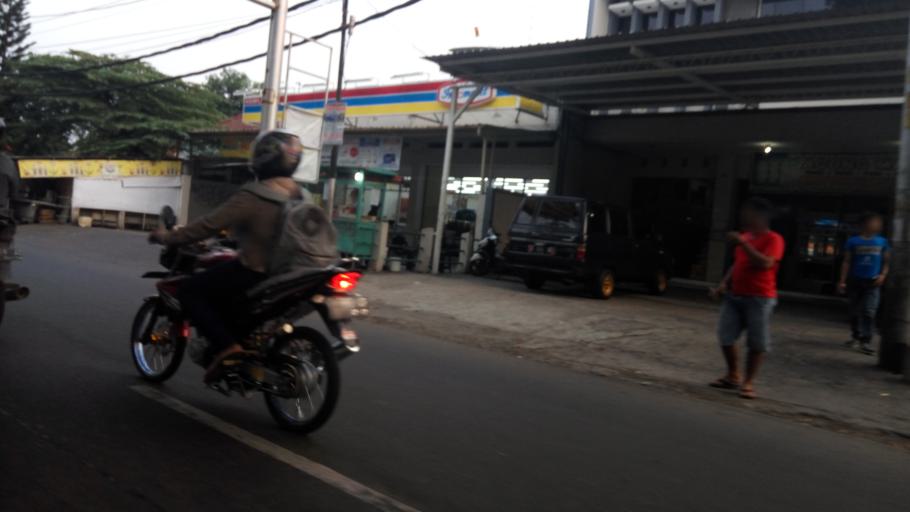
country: ID
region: Central Java
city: Semarang
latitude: -6.9926
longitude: 110.3996
